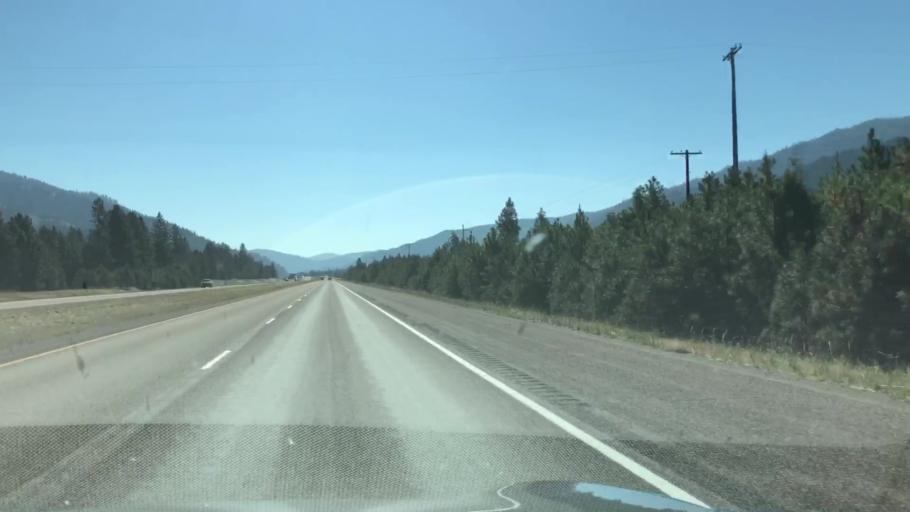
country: US
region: Montana
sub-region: Missoula County
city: Bonner-West Riverside
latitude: 46.8432
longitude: -113.8419
